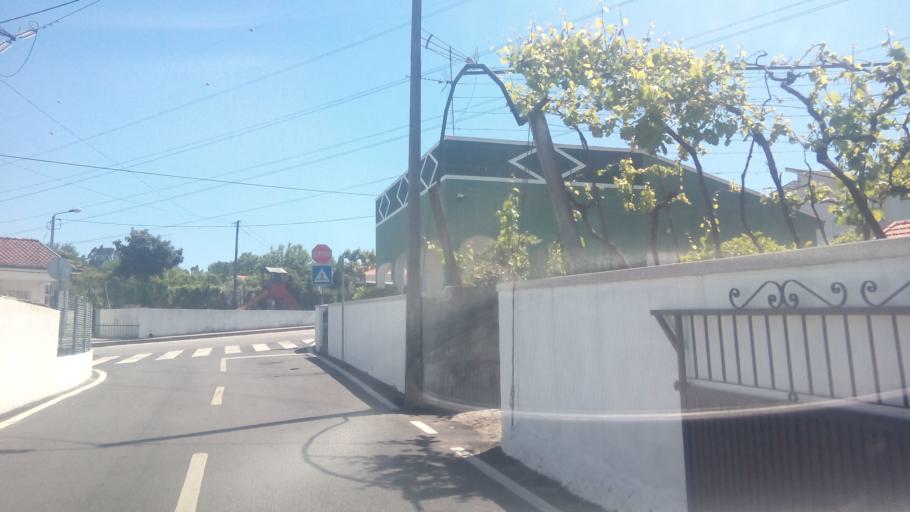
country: PT
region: Porto
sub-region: Paredes
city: Casteloes de Cepeda
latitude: 41.1892
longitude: -8.3379
